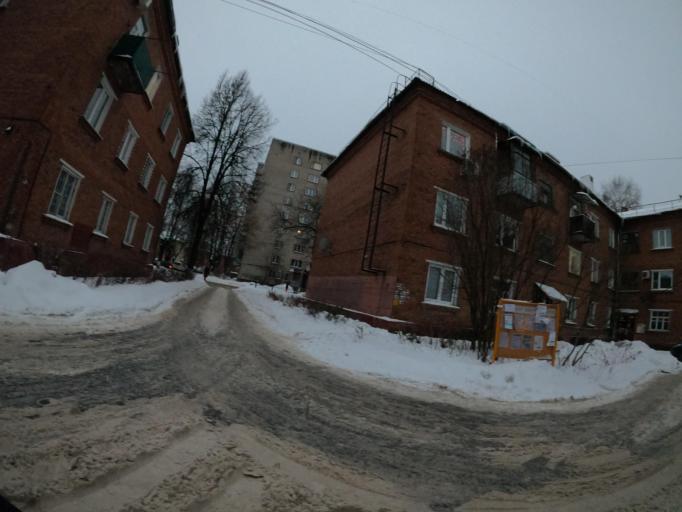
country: RU
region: Moskovskaya
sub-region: Podol'skiy Rayon
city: Podol'sk
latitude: 55.4158
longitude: 37.5316
